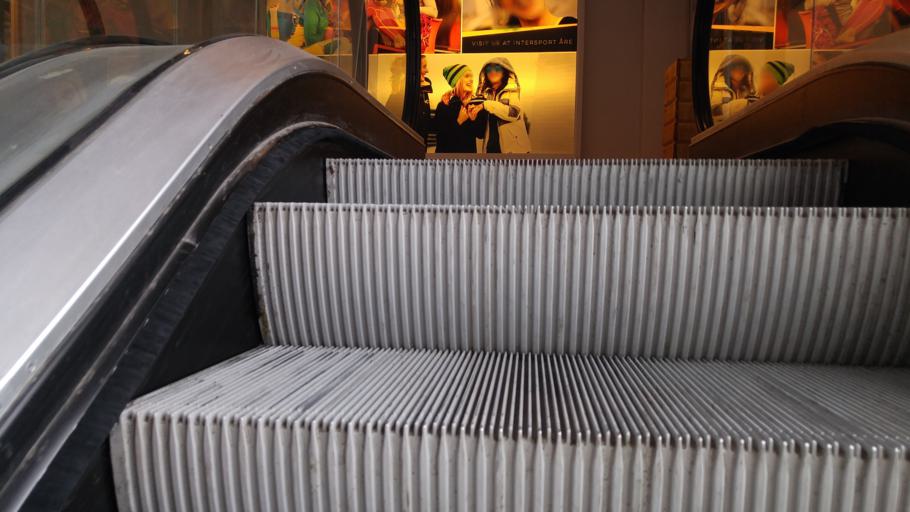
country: SE
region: Jaemtland
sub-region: Are Kommun
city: Are
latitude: 63.3987
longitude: 13.0765
